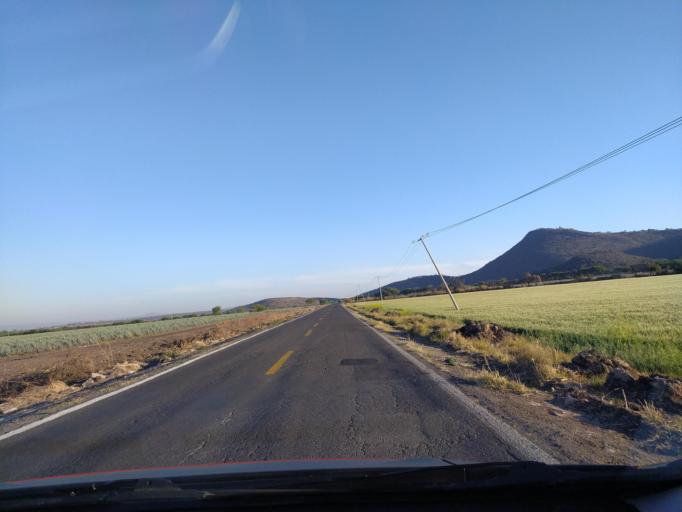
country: MX
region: Guanajuato
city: Ciudad Manuel Doblado
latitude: 20.7826
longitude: -101.8340
